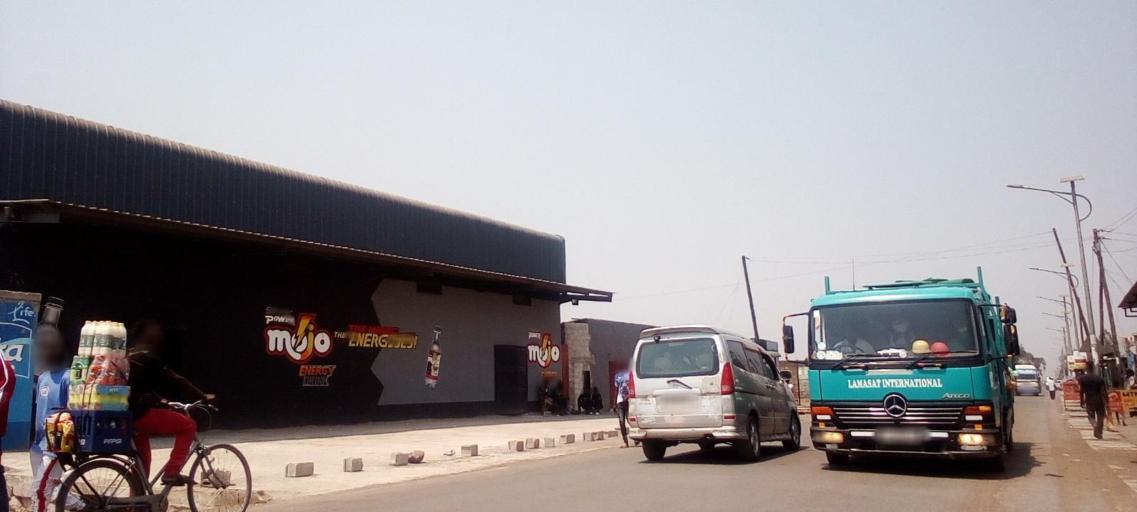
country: ZM
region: Lusaka
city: Lusaka
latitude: -15.4370
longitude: 28.2573
